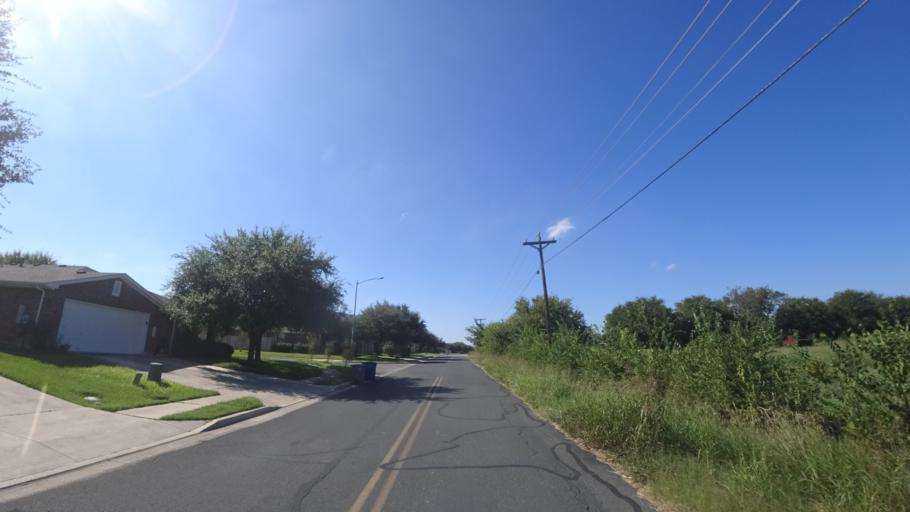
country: US
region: Texas
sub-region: Travis County
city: Manor
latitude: 30.3625
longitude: -97.6082
